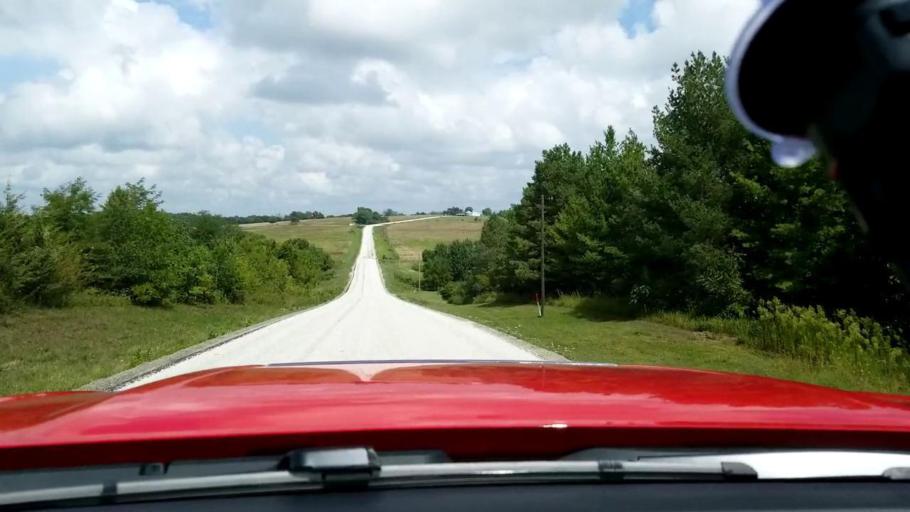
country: US
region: Iowa
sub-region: Decatur County
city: Lamoni
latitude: 40.6469
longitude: -94.0529
